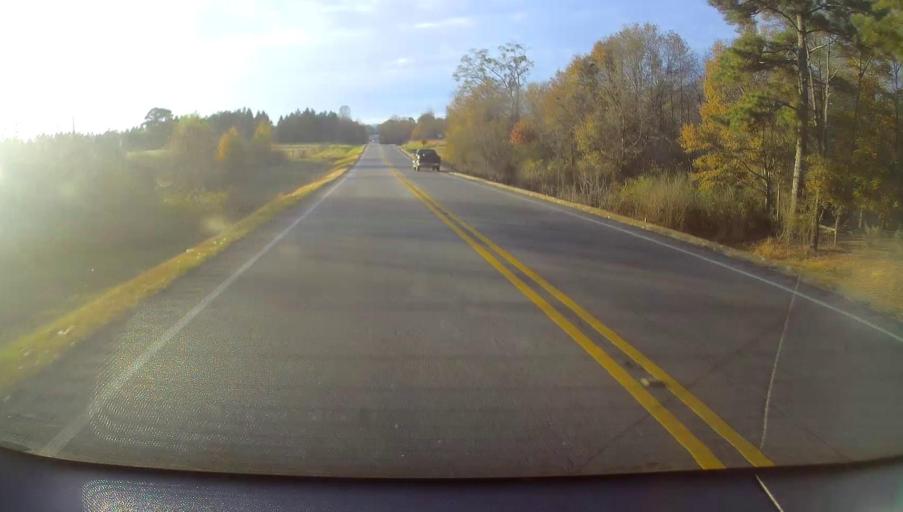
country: US
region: Alabama
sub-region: Blount County
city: Blountsville
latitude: 34.1351
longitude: -86.4241
